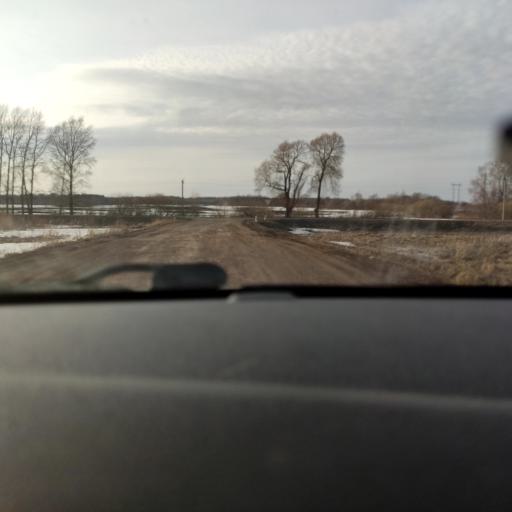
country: RU
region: Bashkortostan
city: Avdon
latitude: 54.4869
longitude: 55.5908
